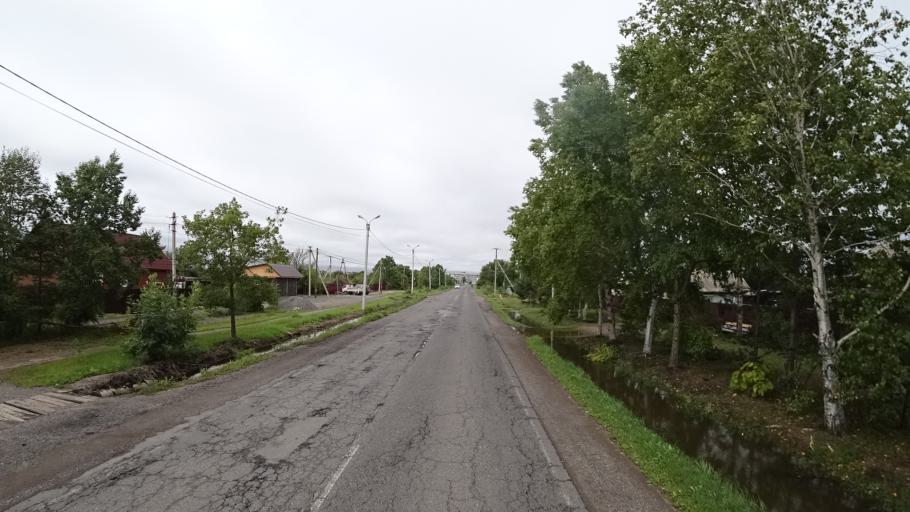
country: RU
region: Primorskiy
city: Monastyrishche
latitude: 44.2017
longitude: 132.4552
